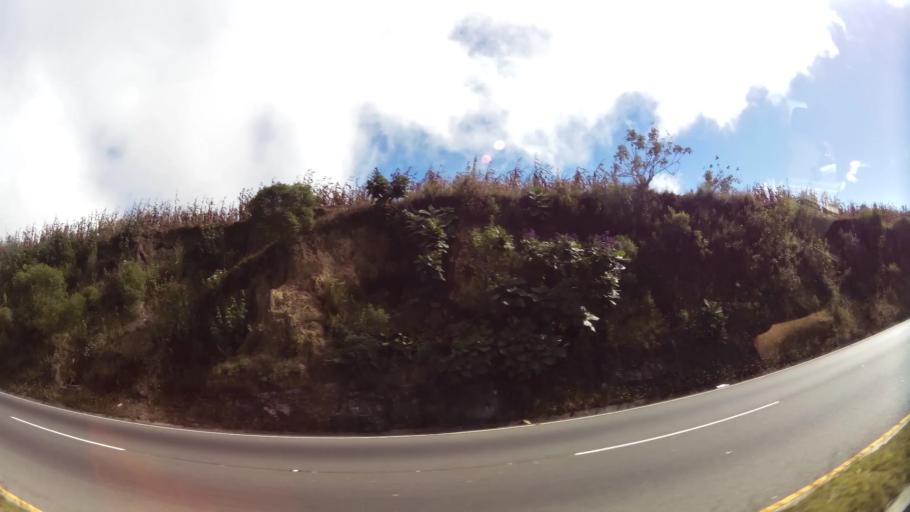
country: GT
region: Solola
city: Santa Catarina Ixtahuacan
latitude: 14.8367
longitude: -91.3637
